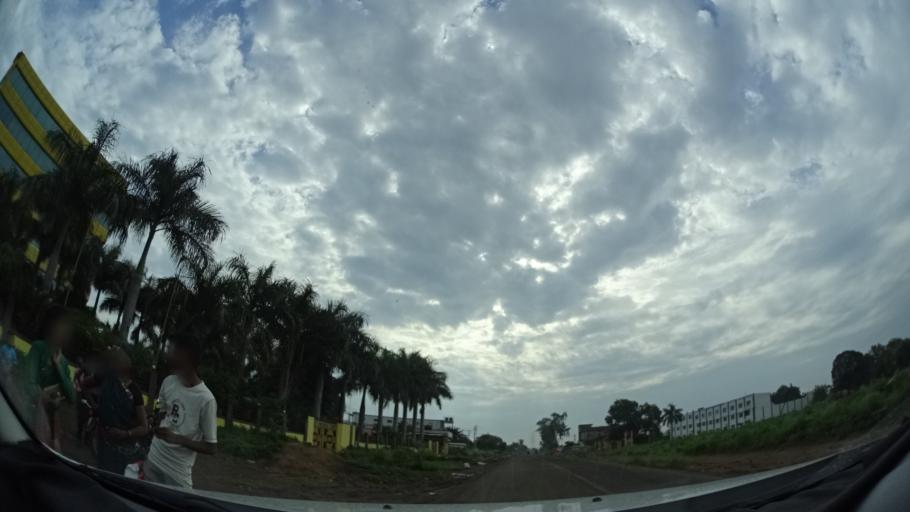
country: IN
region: Madhya Pradesh
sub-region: Bhopal
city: Bhopal
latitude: 23.2517
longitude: 77.5294
